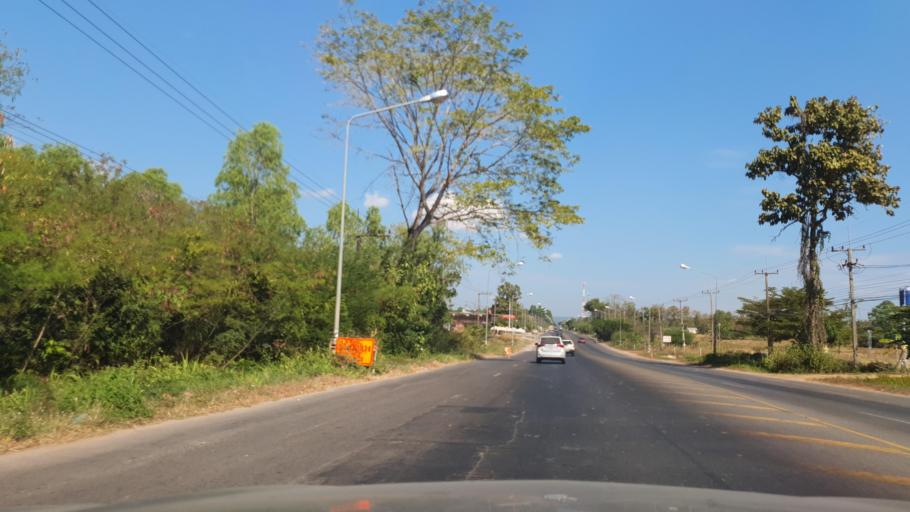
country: TH
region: Kalasin
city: Somdet
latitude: 16.7161
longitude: 103.7553
